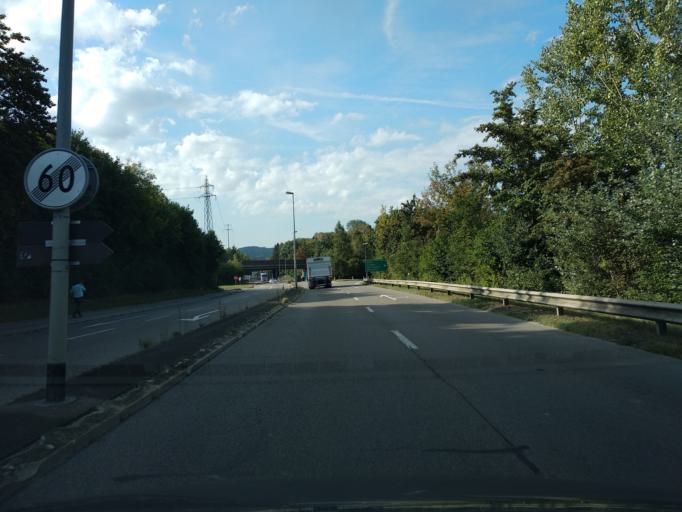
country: CH
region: Thurgau
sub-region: Frauenfeld District
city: Frauenfeld
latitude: 47.5625
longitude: 8.8704
